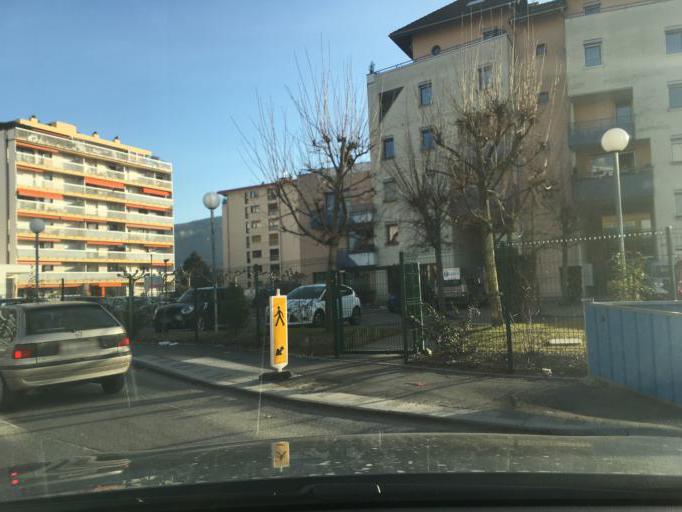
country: FR
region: Rhone-Alpes
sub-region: Departement de la Haute-Savoie
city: Gaillard
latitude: 46.1913
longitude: 6.2145
